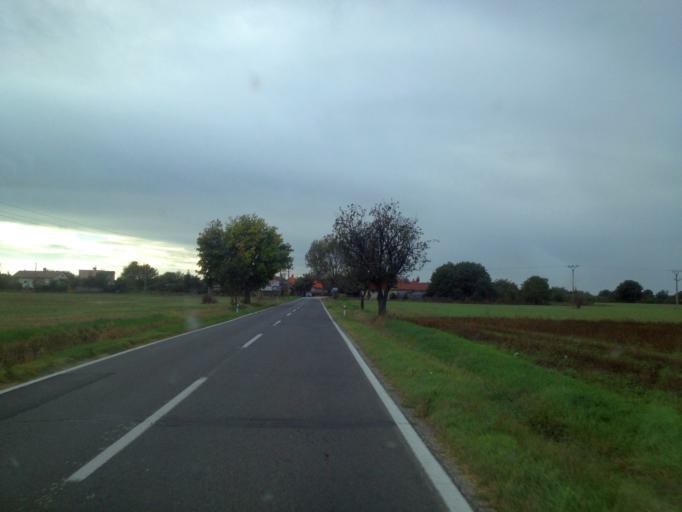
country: HU
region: Komarom-Esztergom
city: Tat
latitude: 47.7901
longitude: 18.6147
